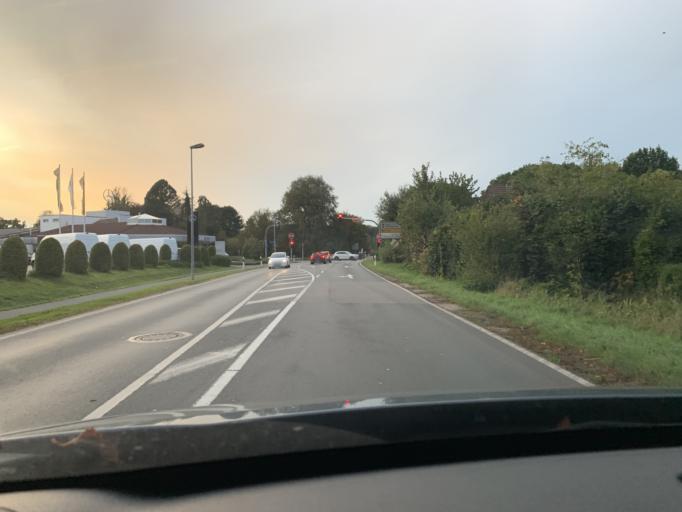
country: DE
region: Lower Saxony
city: Westerstede
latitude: 53.2515
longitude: 7.9162
